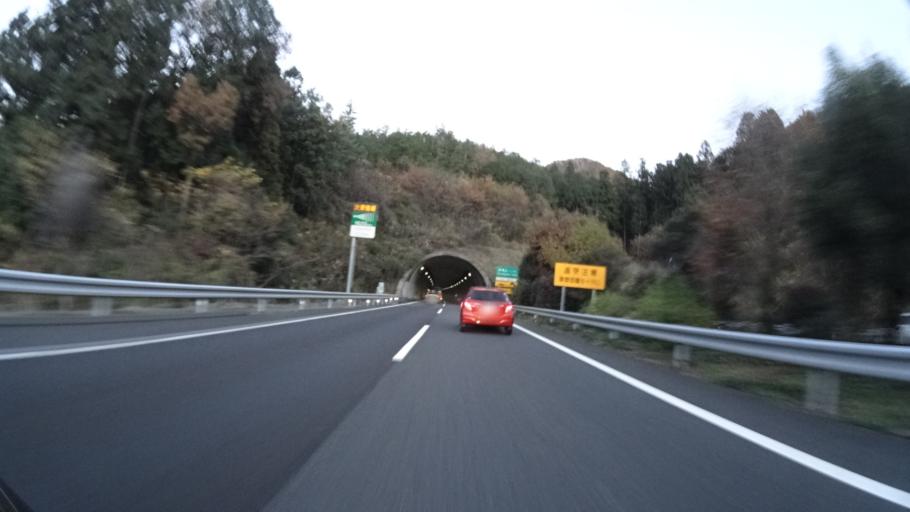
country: JP
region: Ibaraki
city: Kasama
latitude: 36.3399
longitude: 140.2323
